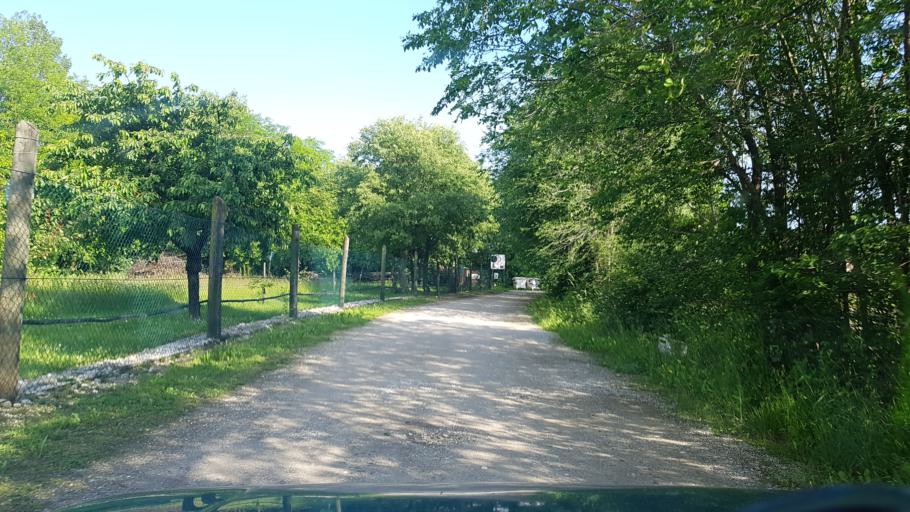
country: IT
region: Friuli Venezia Giulia
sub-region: Provincia di Gorizia
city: Romans d'Isonzo
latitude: 45.8841
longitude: 13.4583
